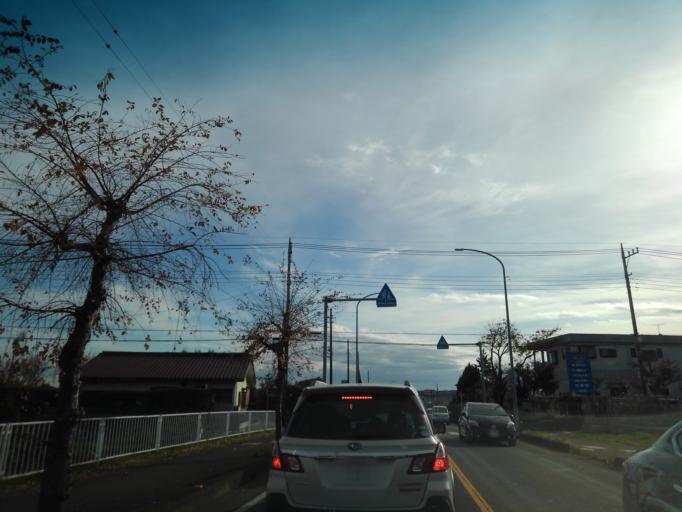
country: JP
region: Saitama
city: Hanno
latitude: 35.8603
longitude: 139.3365
